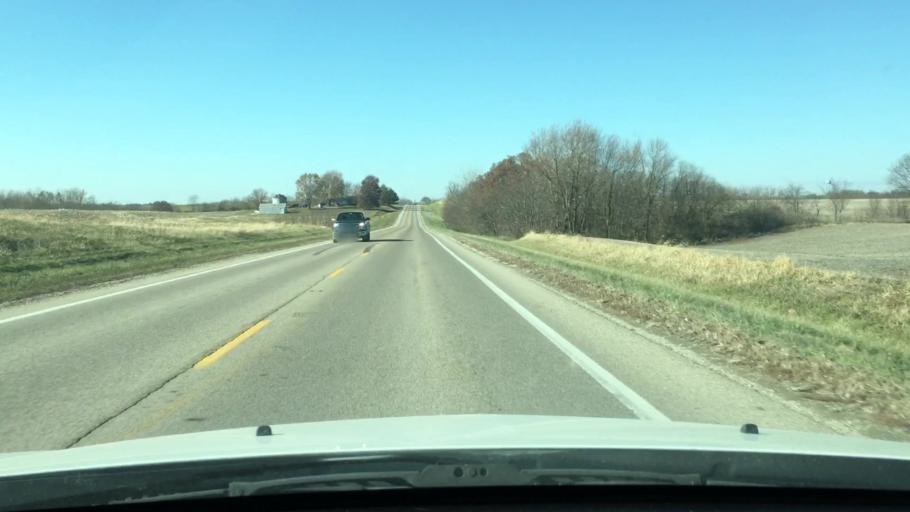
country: US
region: Illinois
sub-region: Pike County
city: Pittsfield
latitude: 39.6050
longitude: -90.8645
